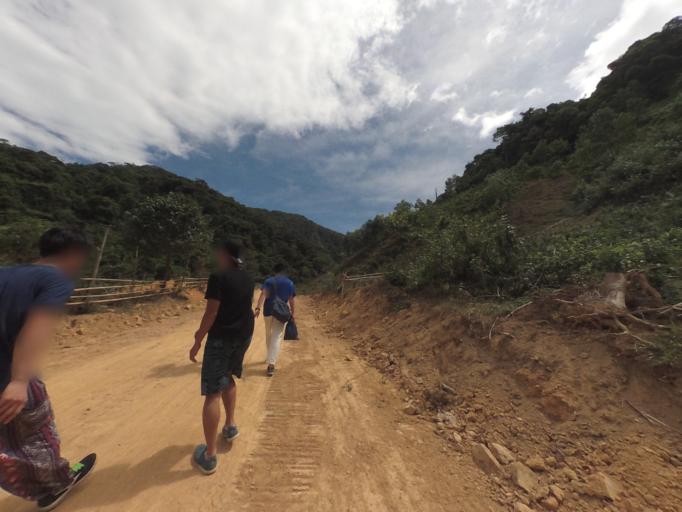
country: VN
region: Thua Thien-Hue
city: A Luoi
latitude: 16.3061
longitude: 107.2158
